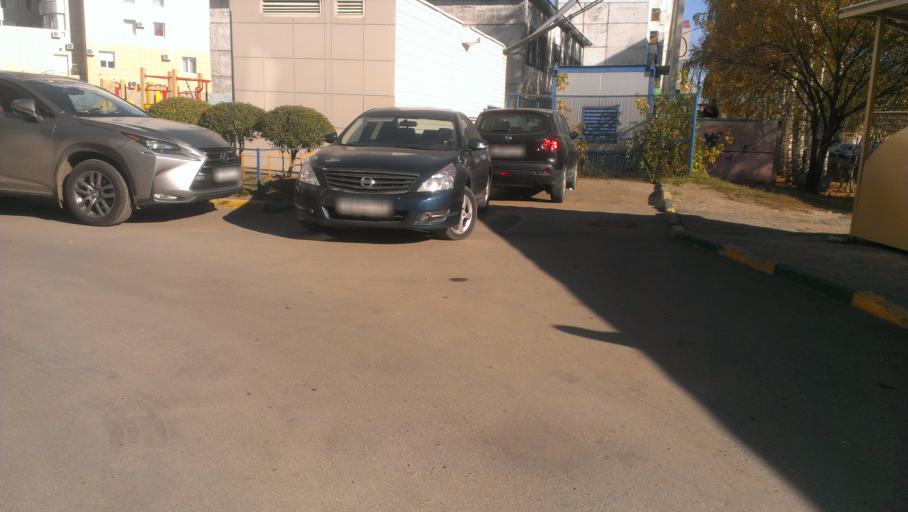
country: RU
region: Altai Krai
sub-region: Gorod Barnaulskiy
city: Barnaul
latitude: 53.3405
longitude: 83.6979
